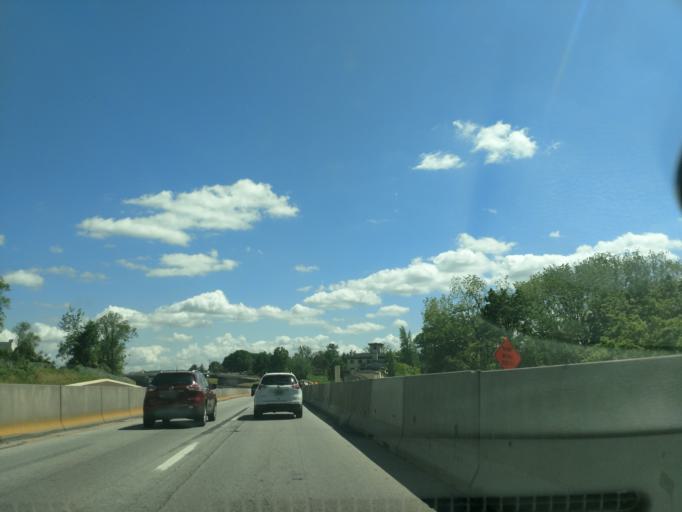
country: US
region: Pennsylvania
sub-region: Montgomery County
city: Audubon
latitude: 40.1056
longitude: -75.4201
